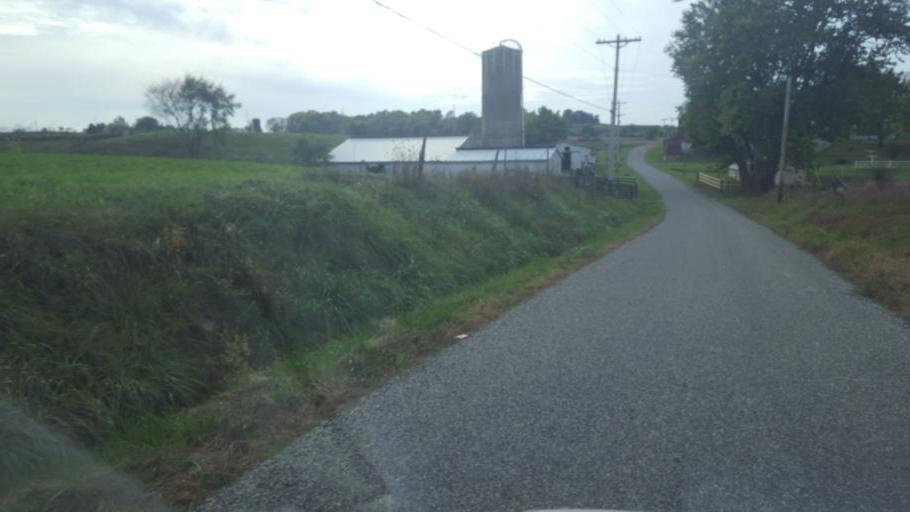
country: US
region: Ohio
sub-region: Holmes County
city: Millersburg
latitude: 40.5846
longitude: -81.8462
